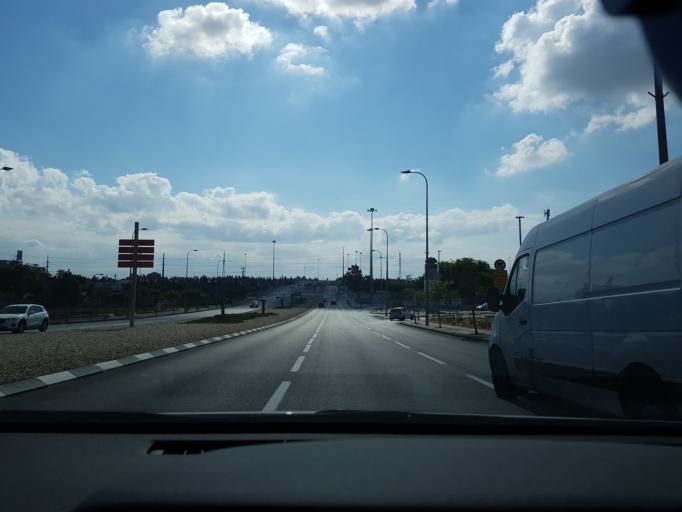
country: IL
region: Tel Aviv
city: Azor
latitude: 32.0048
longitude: 34.8000
